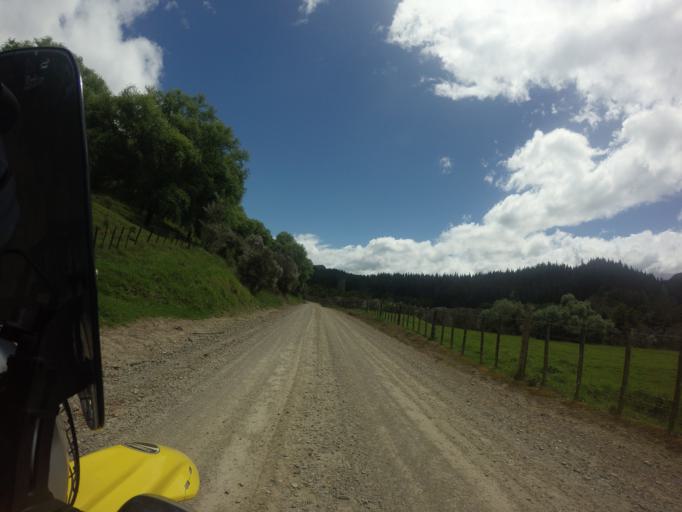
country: NZ
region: Hawke's Bay
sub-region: Wairoa District
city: Wairoa
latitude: -38.9870
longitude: 177.7560
